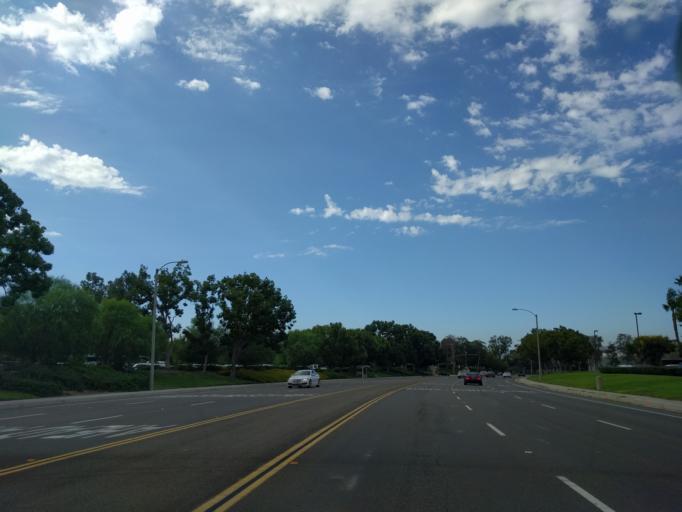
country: US
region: California
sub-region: Orange County
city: Lake Forest
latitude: 33.6564
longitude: -117.7112
